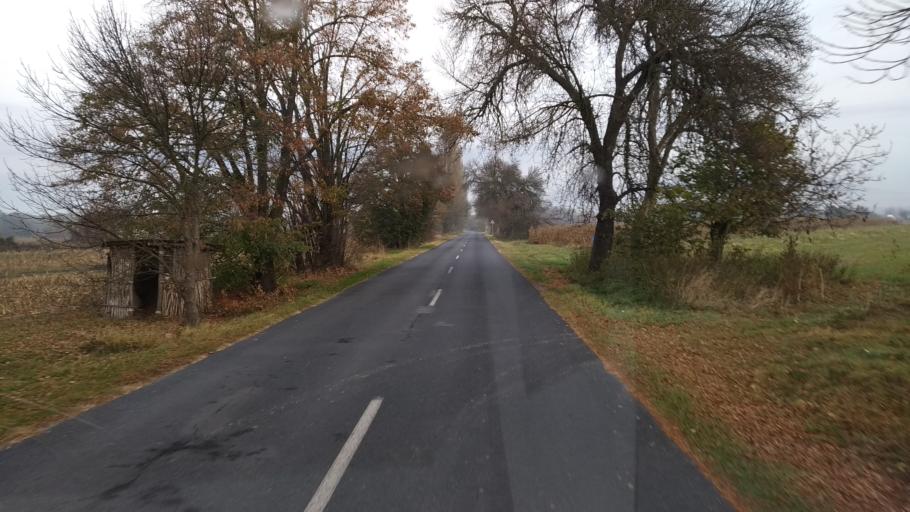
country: HU
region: Pest
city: Tahitotfalu
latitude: 47.7644
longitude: 19.0863
